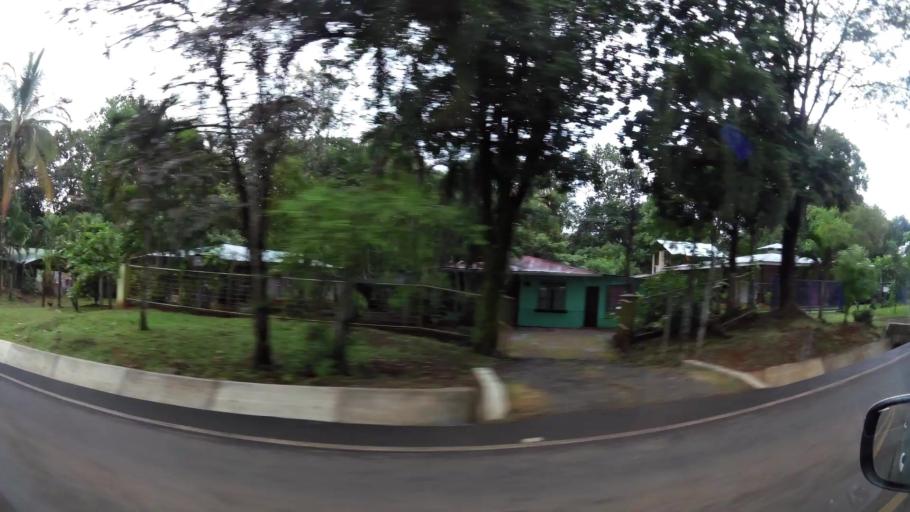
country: CR
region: Alajuela
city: Orotina
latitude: 9.9548
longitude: -84.5797
